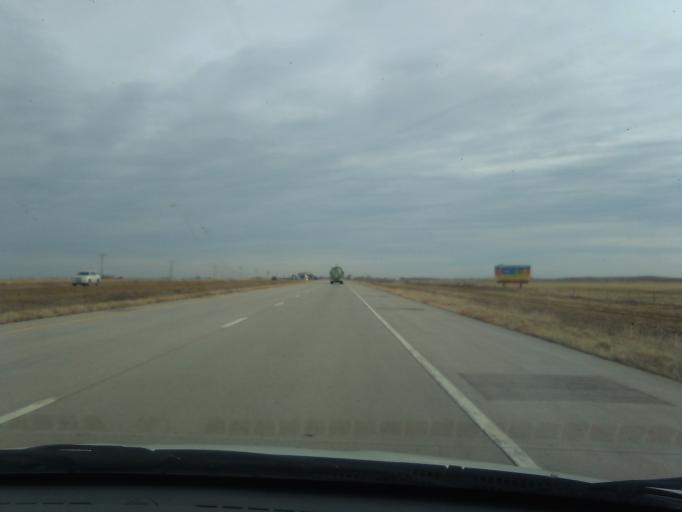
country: US
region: Colorado
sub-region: Morgan County
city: Fort Morgan
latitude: 40.2319
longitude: -104.1252
